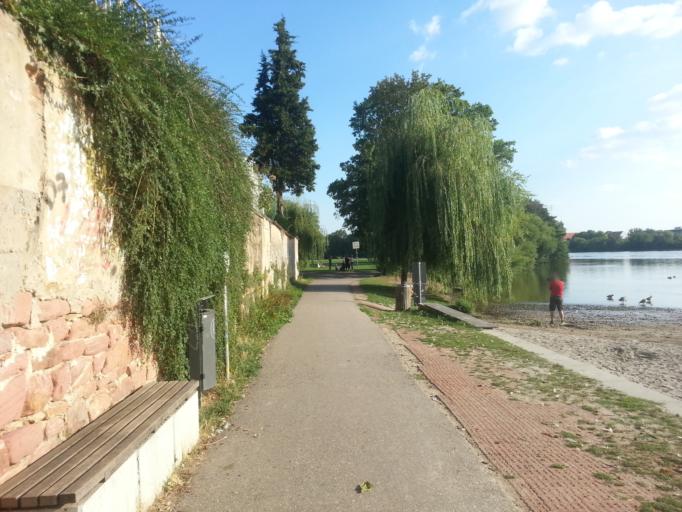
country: DE
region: Baden-Wuerttemberg
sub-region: Karlsruhe Region
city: Ladenburg
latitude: 49.4685
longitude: 8.6057
